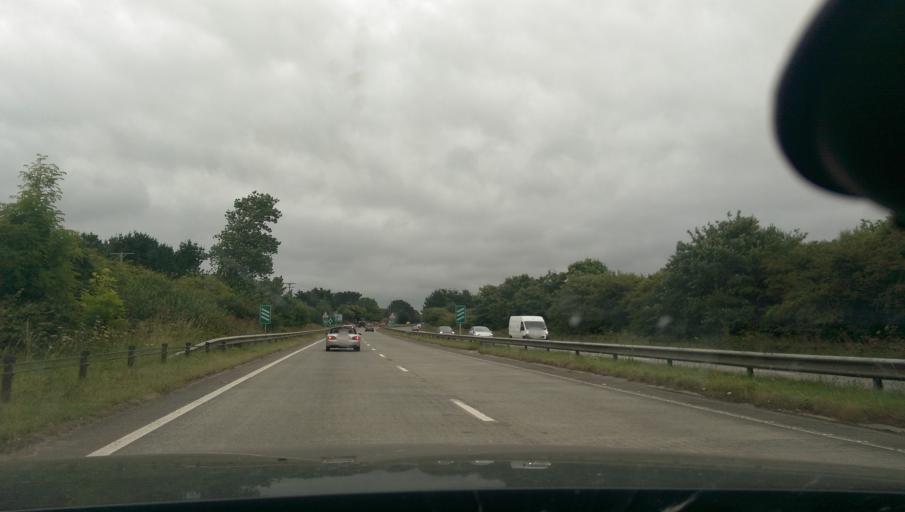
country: GB
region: England
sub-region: Cornwall
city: Marazion
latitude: 50.1341
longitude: -5.4955
